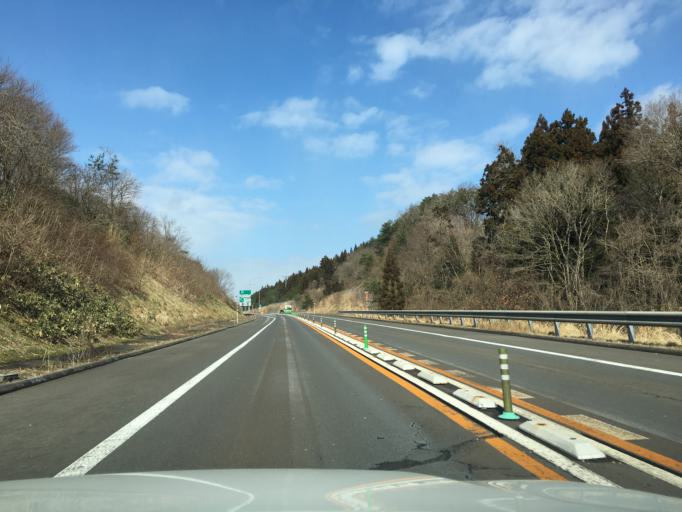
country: JP
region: Akita
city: Akita
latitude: 39.7461
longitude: 140.1577
